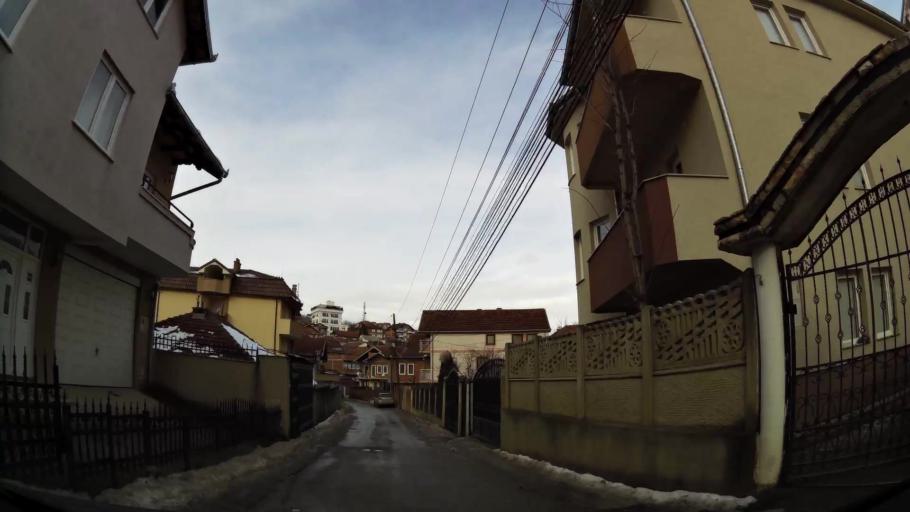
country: XK
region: Pristina
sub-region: Komuna e Prishtines
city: Pristina
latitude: 42.6710
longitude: 21.1868
